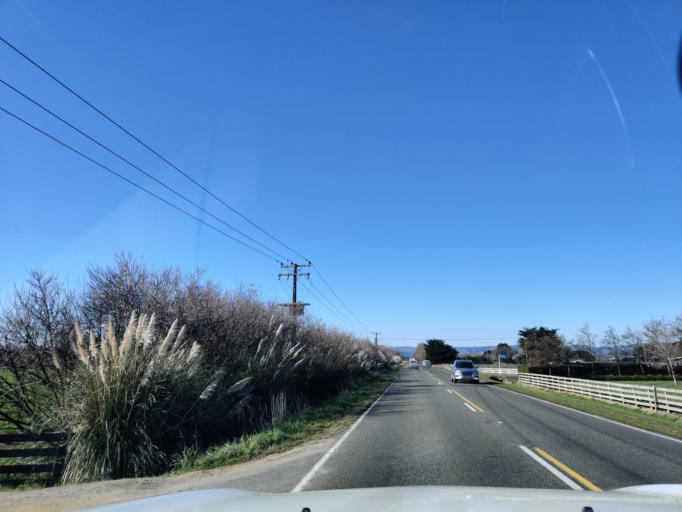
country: NZ
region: Manawatu-Wanganui
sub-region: Palmerston North City
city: Palmerston North
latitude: -40.3116
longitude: 175.5918
